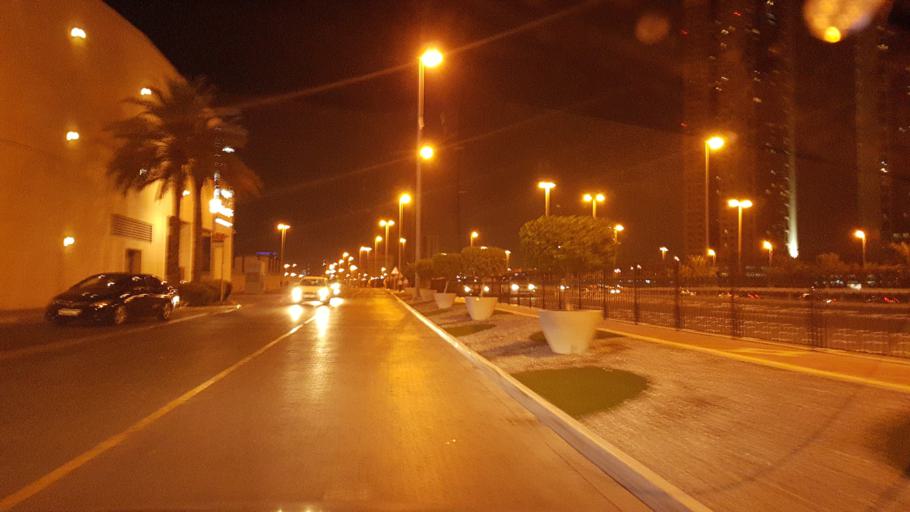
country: BH
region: Manama
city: Jidd Hafs
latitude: 26.2323
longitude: 50.5554
